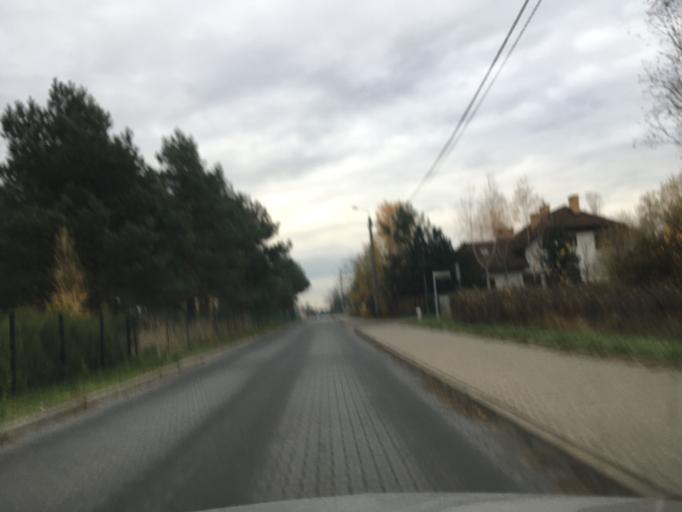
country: PL
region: Masovian Voivodeship
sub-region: Powiat piaseczynski
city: Lesznowola
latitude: 52.0745
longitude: 20.9231
